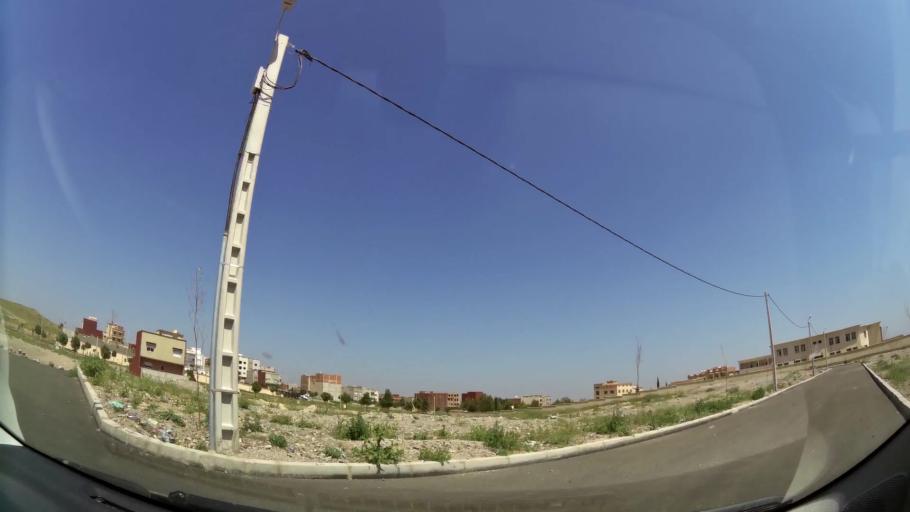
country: MA
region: Oriental
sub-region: Oujda-Angad
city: Oujda
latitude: 34.6787
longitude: -1.9455
